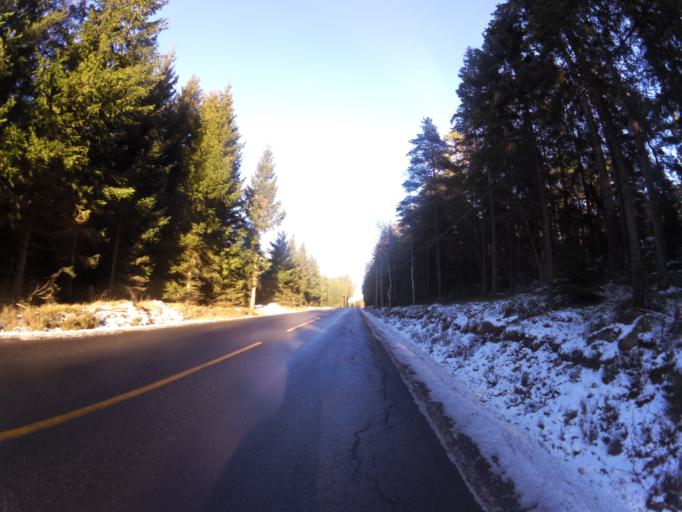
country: NO
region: Ostfold
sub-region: Fredrikstad
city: Lervik
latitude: 59.2278
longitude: 10.8068
